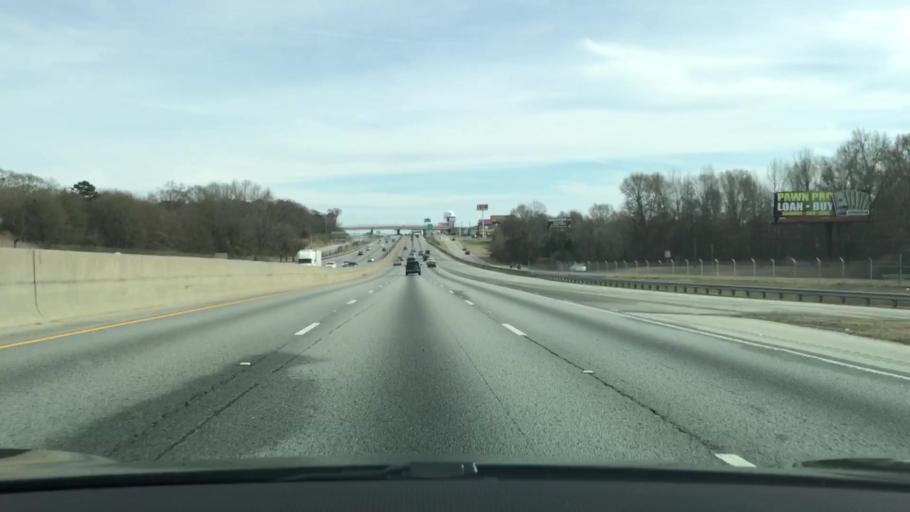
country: US
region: Georgia
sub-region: Rockdale County
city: Conyers
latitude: 33.6636
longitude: -84.0276
